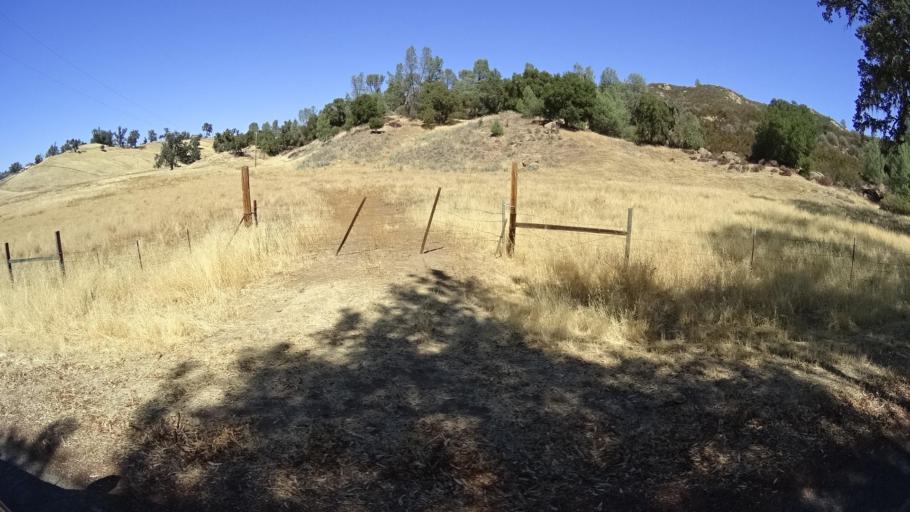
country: US
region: California
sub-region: San Luis Obispo County
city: Lake Nacimiento
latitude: 35.8143
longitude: -121.0927
